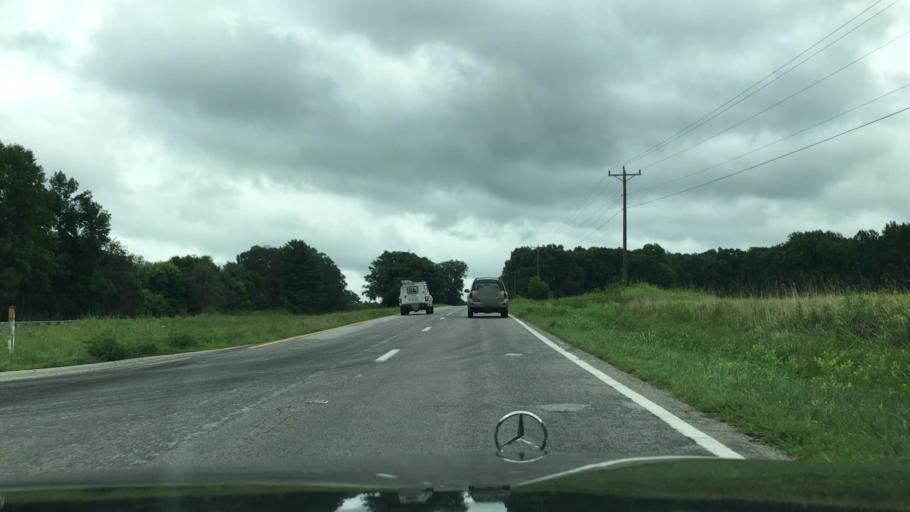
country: US
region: Virginia
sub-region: Prince Edward County
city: Hampden Sydney
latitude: 37.3067
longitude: -78.5159
